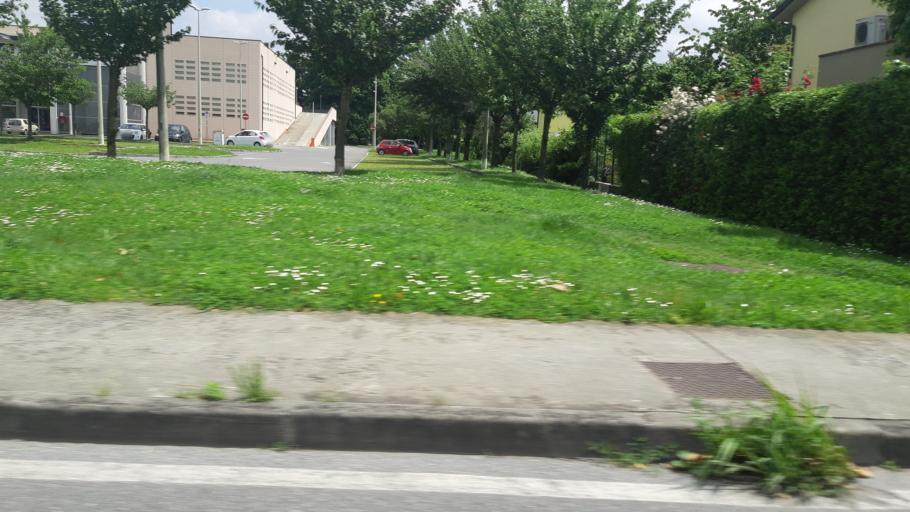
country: IT
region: Tuscany
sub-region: Provincia di Lucca
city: Capannori
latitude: 43.8516
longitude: 10.5251
